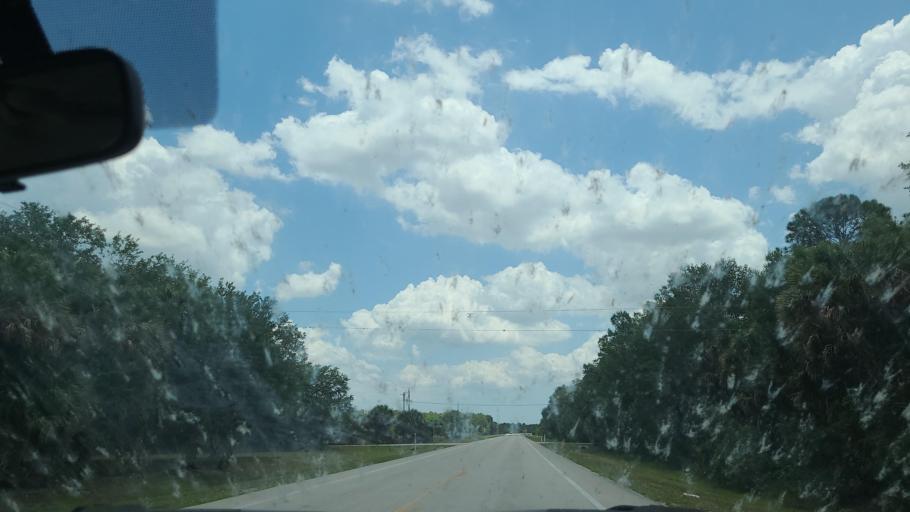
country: US
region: Florida
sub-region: Glades County
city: Buckhead Ridge
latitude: 27.1176
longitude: -81.0767
